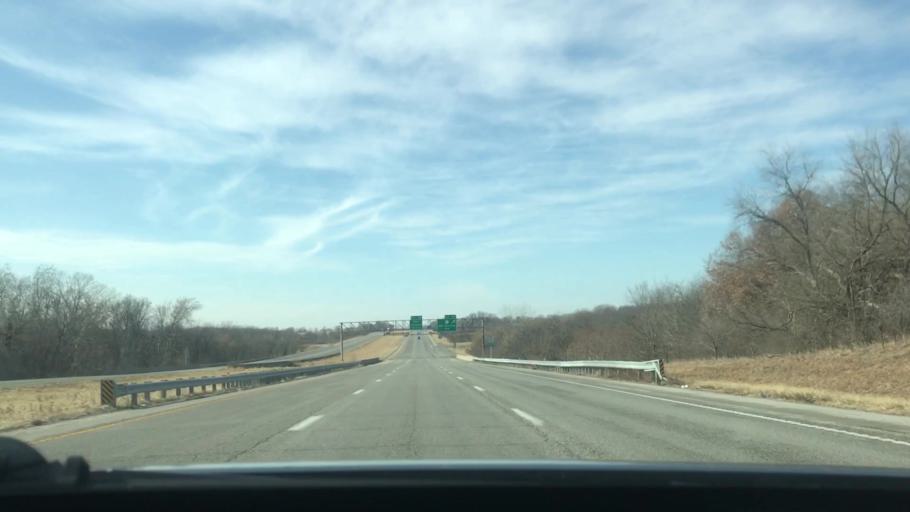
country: US
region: Missouri
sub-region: Platte County
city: Weatherby Lake
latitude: 39.3077
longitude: -94.6404
